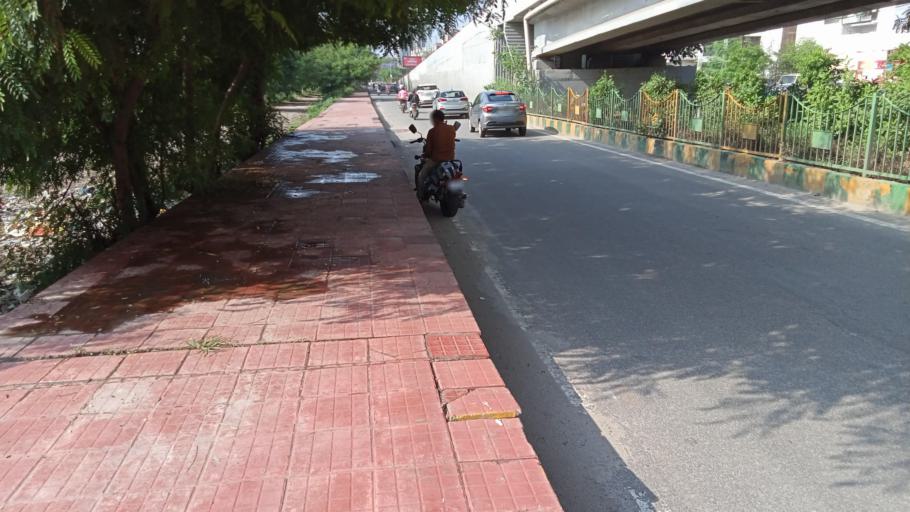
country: IN
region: Uttar Pradesh
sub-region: Ghaziabad
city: Ghaziabad
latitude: 28.6596
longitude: 77.3750
